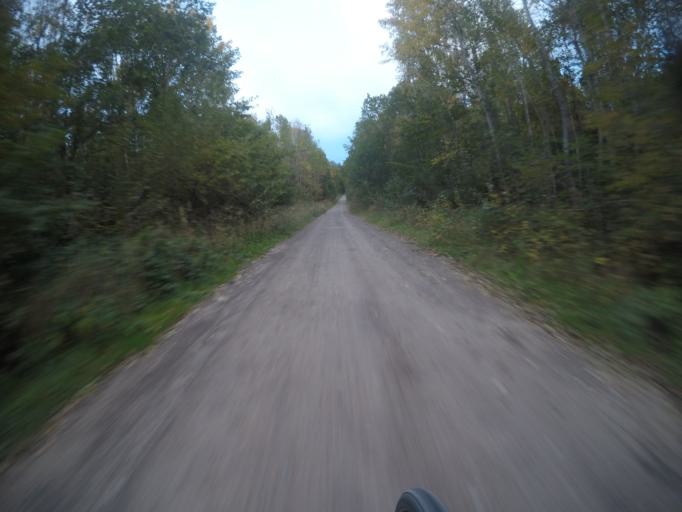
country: DE
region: Baden-Wuerttemberg
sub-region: Regierungsbezirk Stuttgart
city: Schonaich
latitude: 48.6936
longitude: 9.0640
